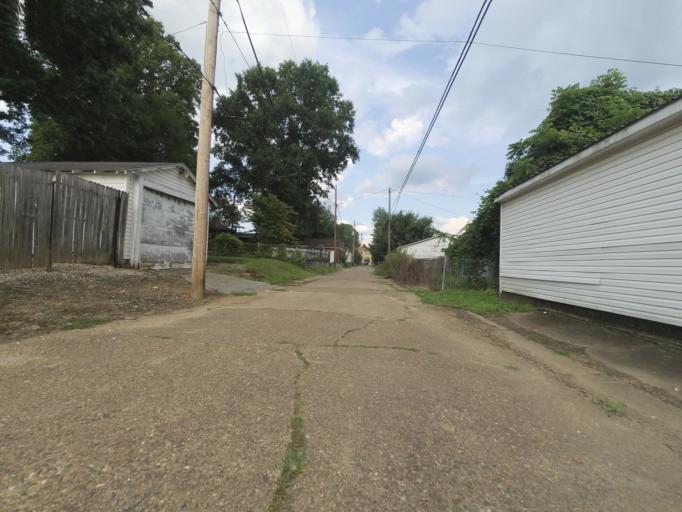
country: US
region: West Virginia
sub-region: Cabell County
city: Huntington
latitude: 38.4302
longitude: -82.4081
